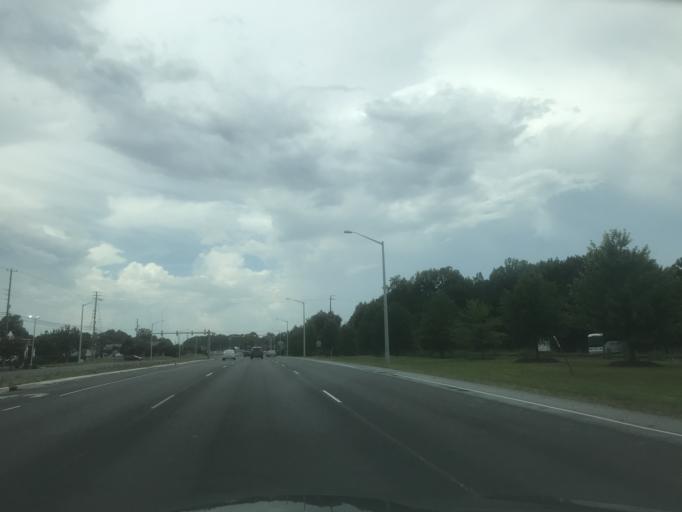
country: US
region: North Carolina
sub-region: Johnston County
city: Clayton
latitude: 35.6392
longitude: -78.4465
